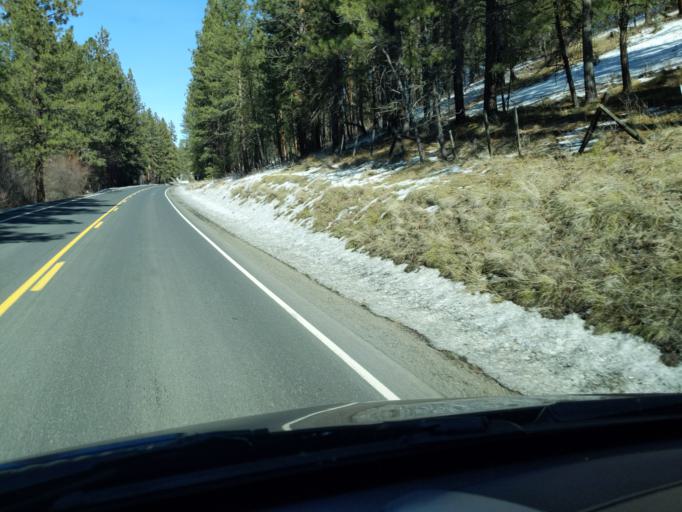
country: US
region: Oregon
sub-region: Grant County
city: John Day
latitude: 44.8725
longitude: -119.0205
